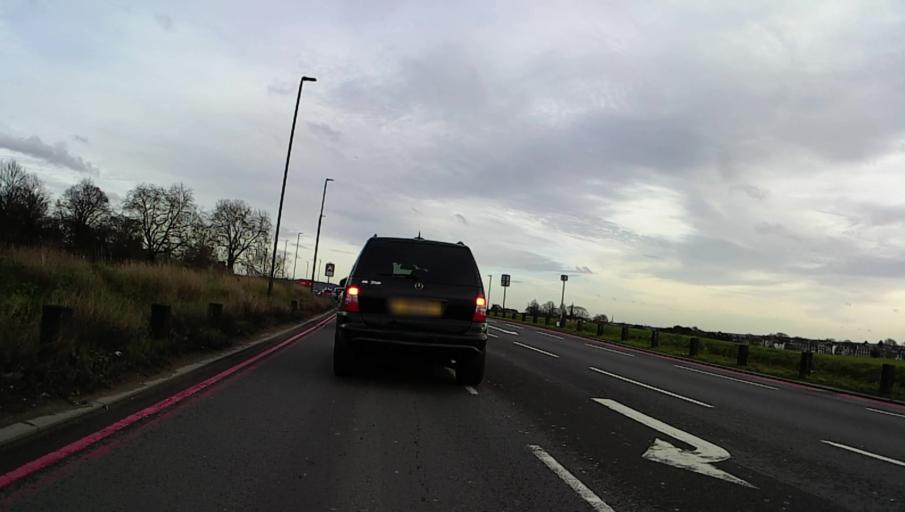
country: GB
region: England
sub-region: Greater London
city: Blackheath
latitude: 51.4720
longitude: -0.0015
